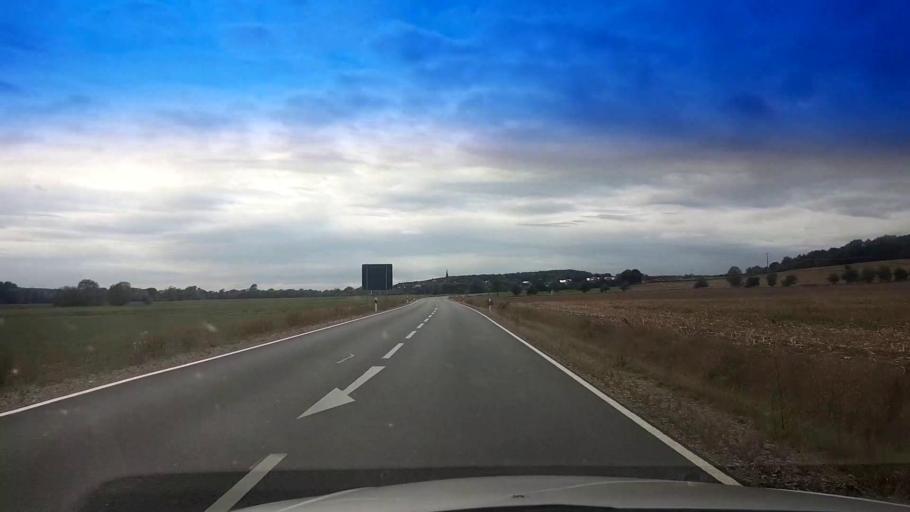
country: DE
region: Bavaria
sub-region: Upper Franconia
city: Frensdorf
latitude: 49.7947
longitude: 10.9029
